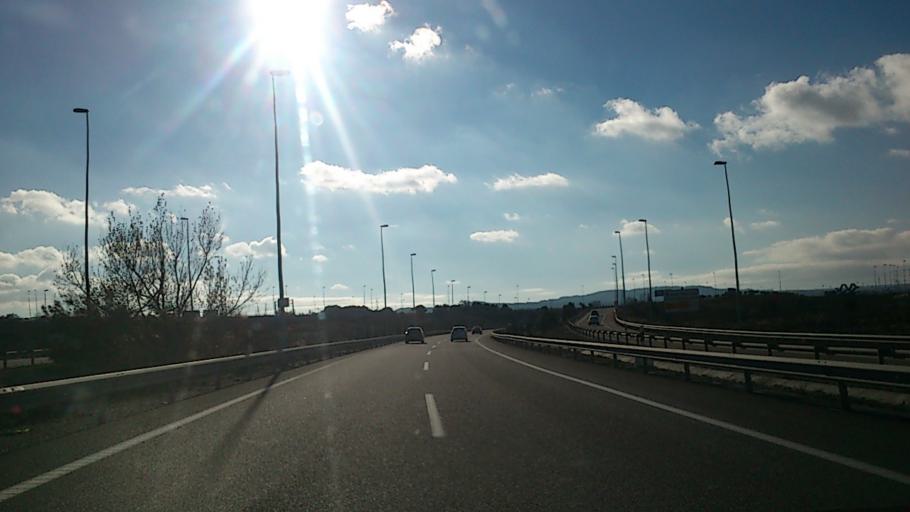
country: ES
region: Aragon
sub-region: Provincia de Zaragoza
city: Montecanal
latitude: 41.6380
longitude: -0.9737
